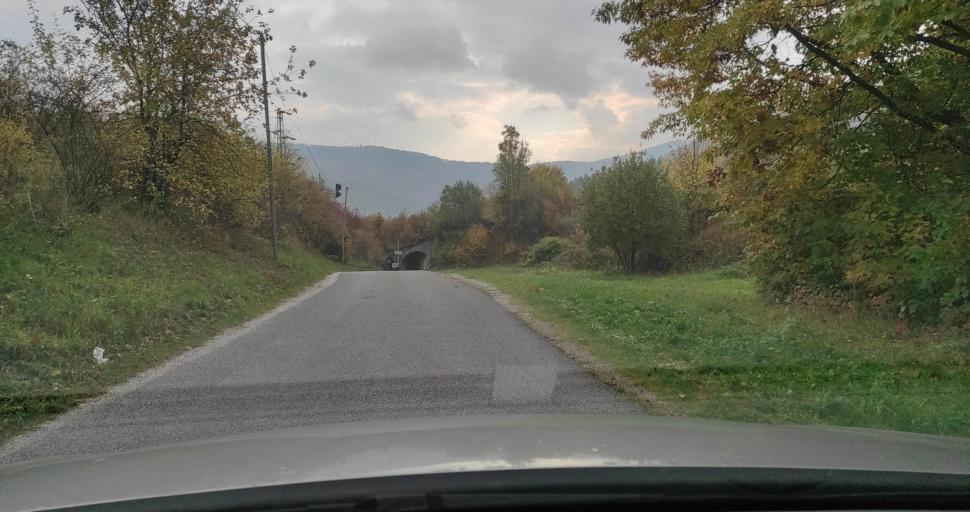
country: SK
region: Kosicky
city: Gelnica
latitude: 48.8925
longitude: 21.0209
